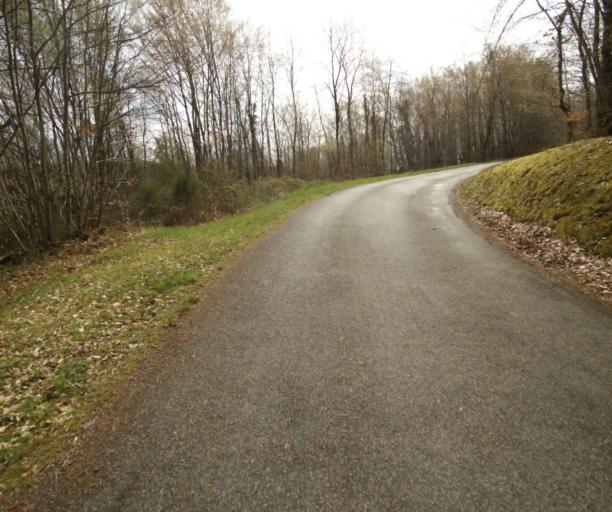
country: FR
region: Limousin
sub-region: Departement de la Correze
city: Laguenne
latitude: 45.2404
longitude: 1.8422
